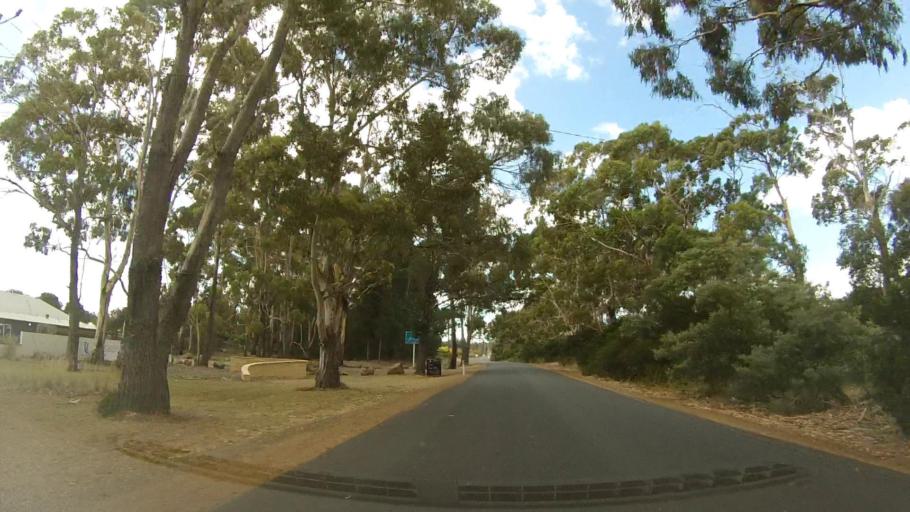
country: AU
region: Tasmania
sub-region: Clarence
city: Seven Mile Beach
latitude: -42.8545
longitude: 147.5133
